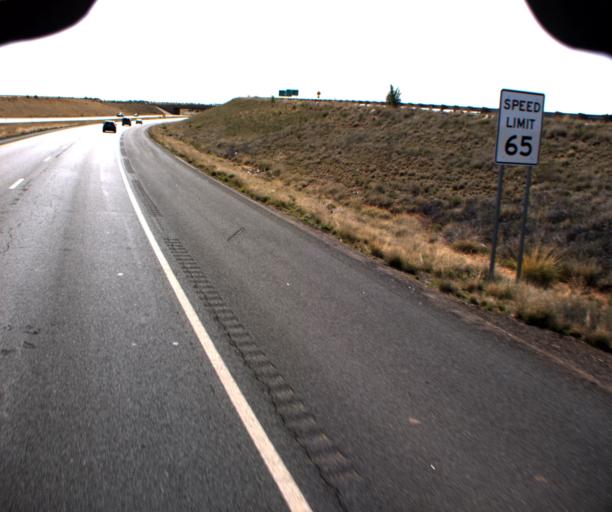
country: US
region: Arizona
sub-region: Yavapai County
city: Prescott Valley
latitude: 34.6371
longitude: -112.4031
